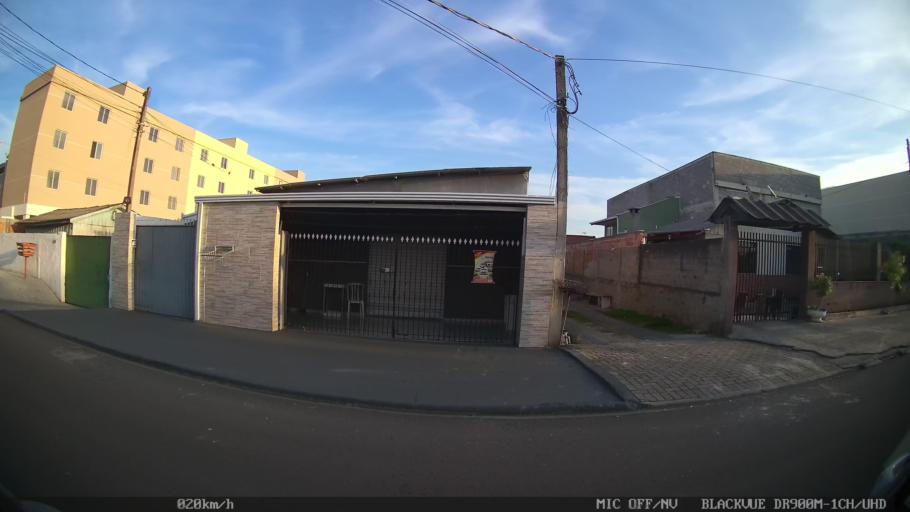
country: BR
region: Parana
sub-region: Pinhais
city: Pinhais
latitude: -25.4500
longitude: -49.1692
